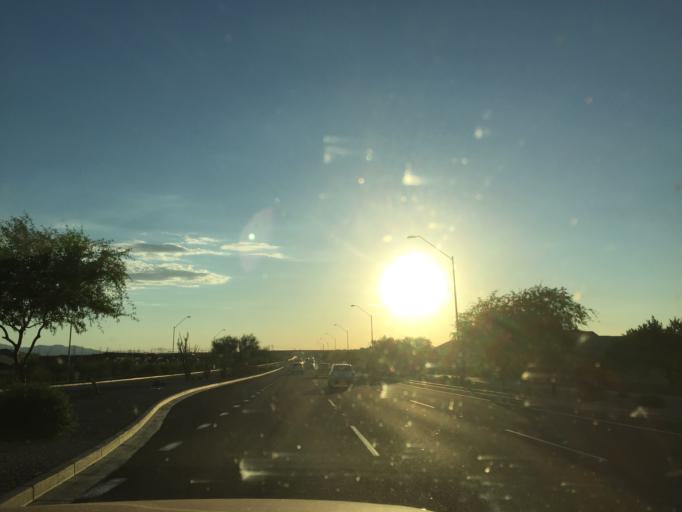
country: US
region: Arizona
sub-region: Maricopa County
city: Sun City West
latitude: 33.7138
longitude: -112.2878
